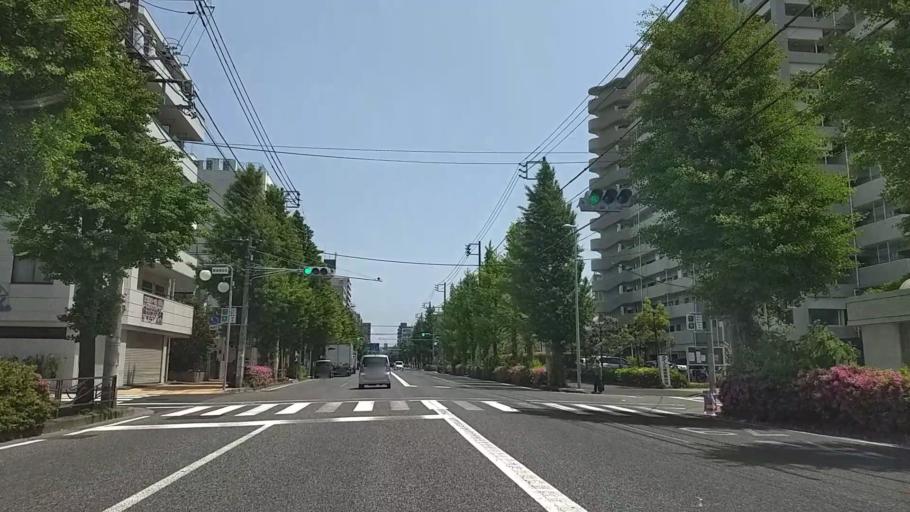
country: JP
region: Kanagawa
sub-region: Kawasaki-shi
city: Kawasaki
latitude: 35.5249
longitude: 139.7199
